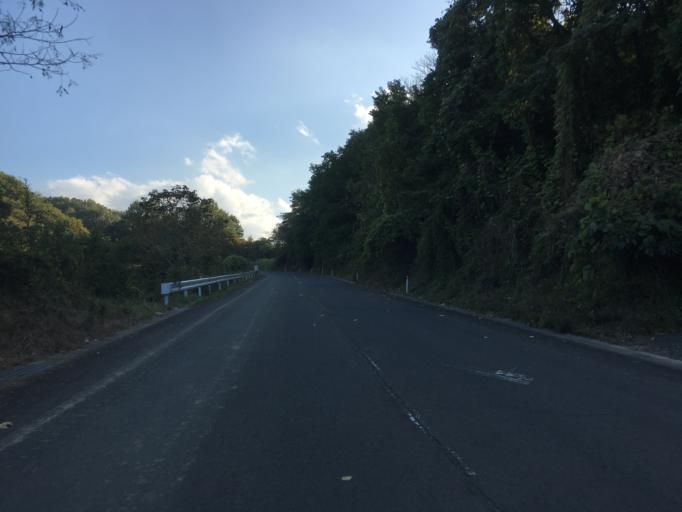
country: JP
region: Fukushima
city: Fukushima-shi
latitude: 37.6542
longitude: 140.5448
